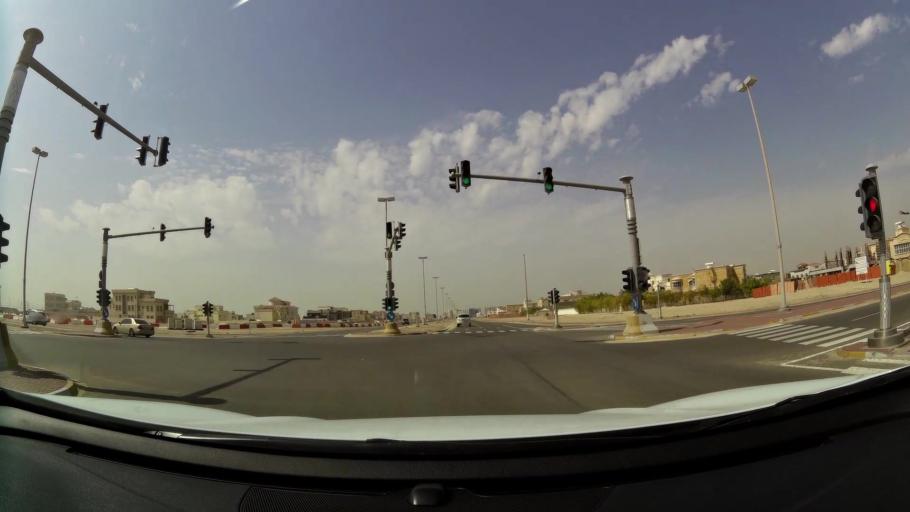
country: AE
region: Abu Dhabi
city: Abu Dhabi
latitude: 24.3065
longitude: 54.5503
